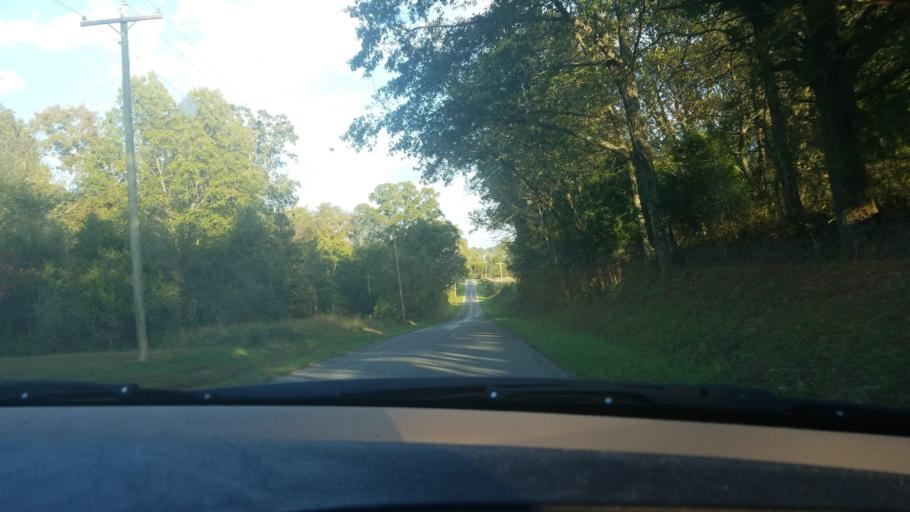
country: US
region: Illinois
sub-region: Saline County
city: Carrier Mills
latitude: 37.7719
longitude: -88.7264
